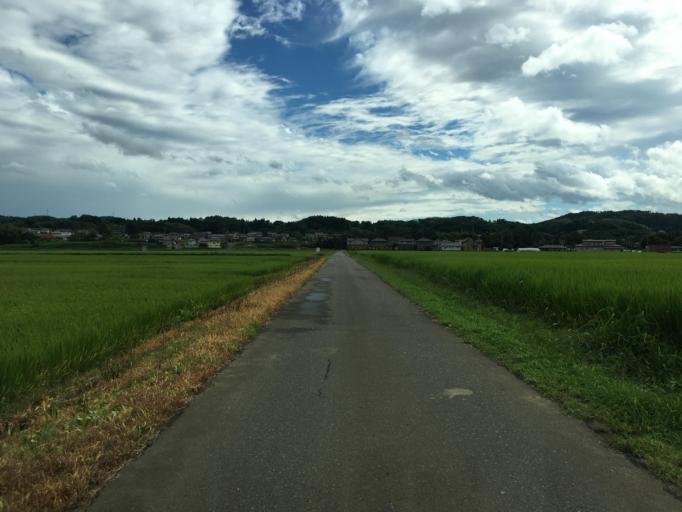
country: JP
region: Fukushima
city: Nihommatsu
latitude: 37.5647
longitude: 140.4194
